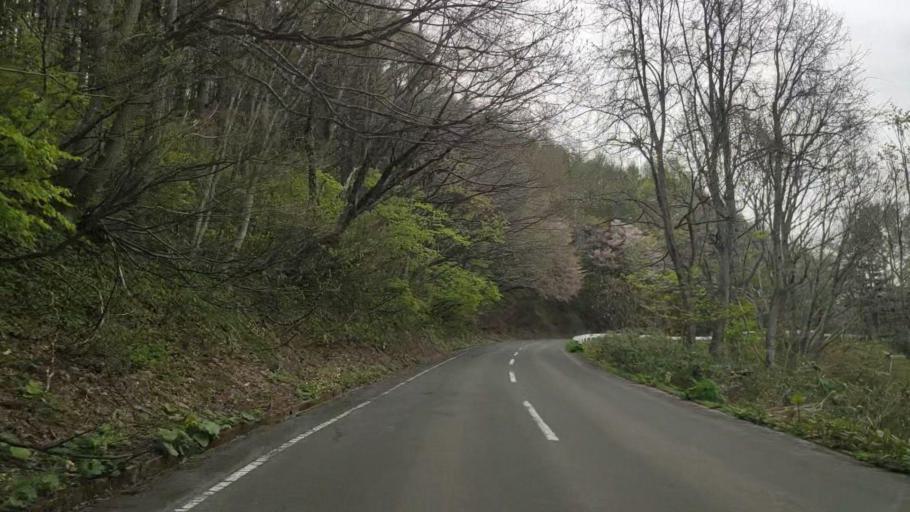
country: JP
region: Aomori
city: Aomori Shi
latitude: 40.7335
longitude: 140.8400
